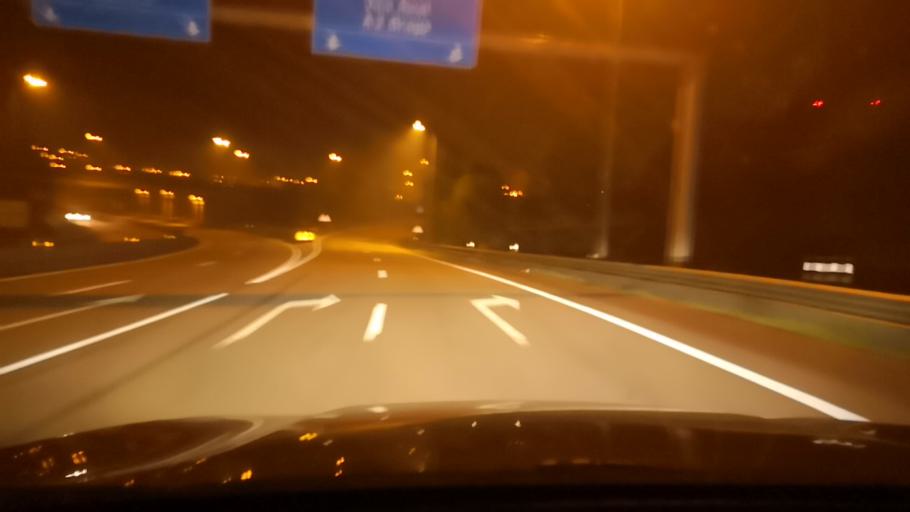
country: PT
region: Porto
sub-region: Maia
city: Leca do Bailio
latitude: 41.2027
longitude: -8.6222
